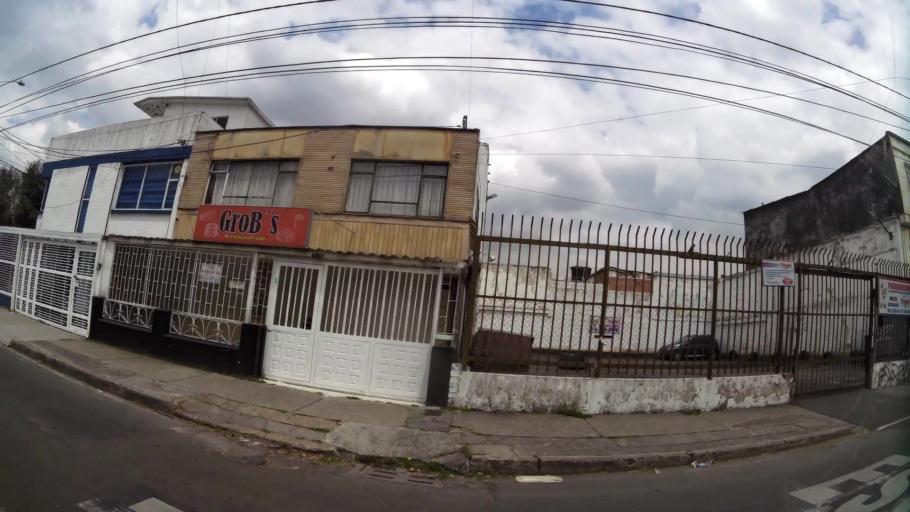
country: CO
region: Bogota D.C.
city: Bogota
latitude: 4.5982
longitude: -74.0986
